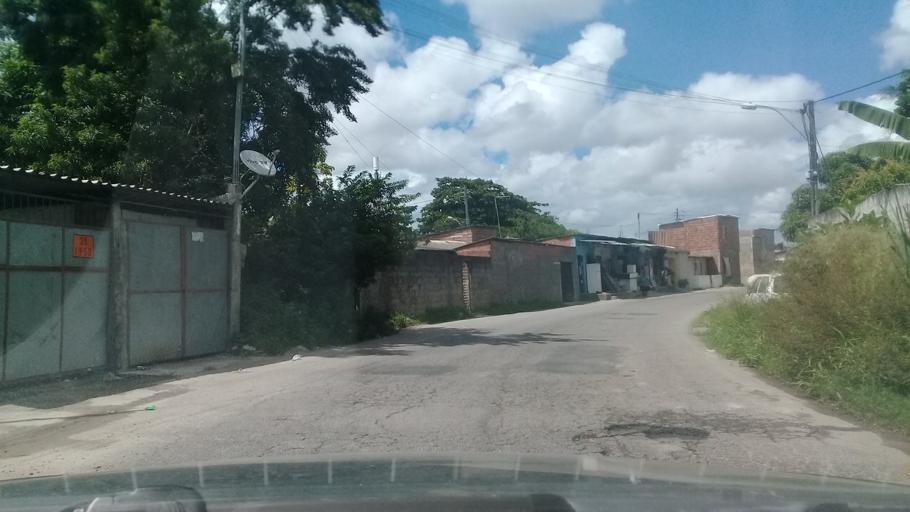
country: BR
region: Pernambuco
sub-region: Recife
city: Recife
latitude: -8.0673
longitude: -34.9385
